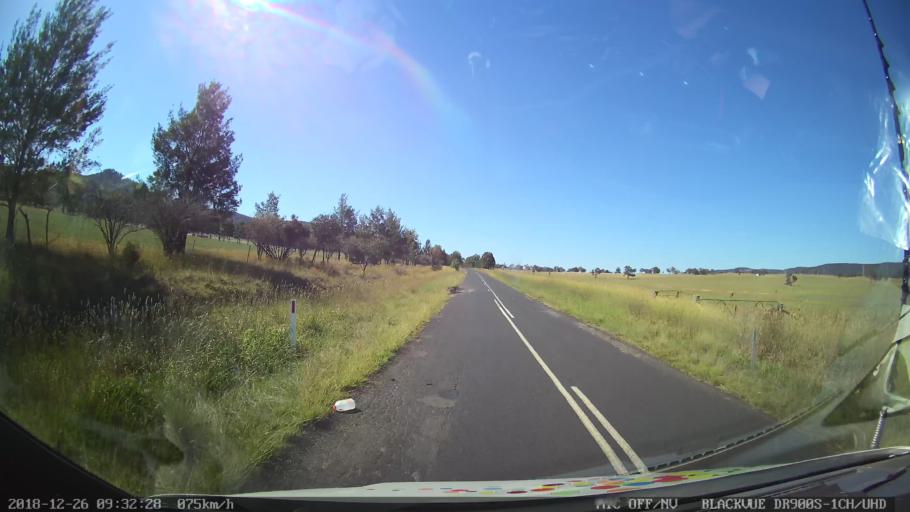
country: AU
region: New South Wales
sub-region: Mid-Western Regional
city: Kandos
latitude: -32.8847
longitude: 150.0324
